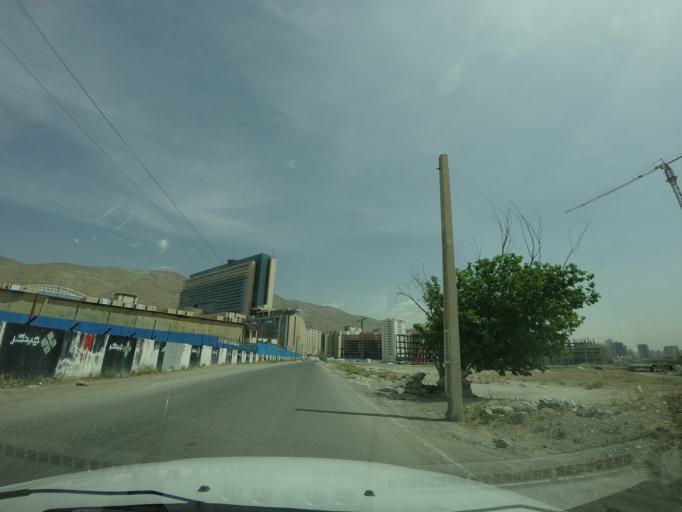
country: IR
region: Tehran
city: Shahr-e Qods
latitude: 35.7506
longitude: 51.1931
